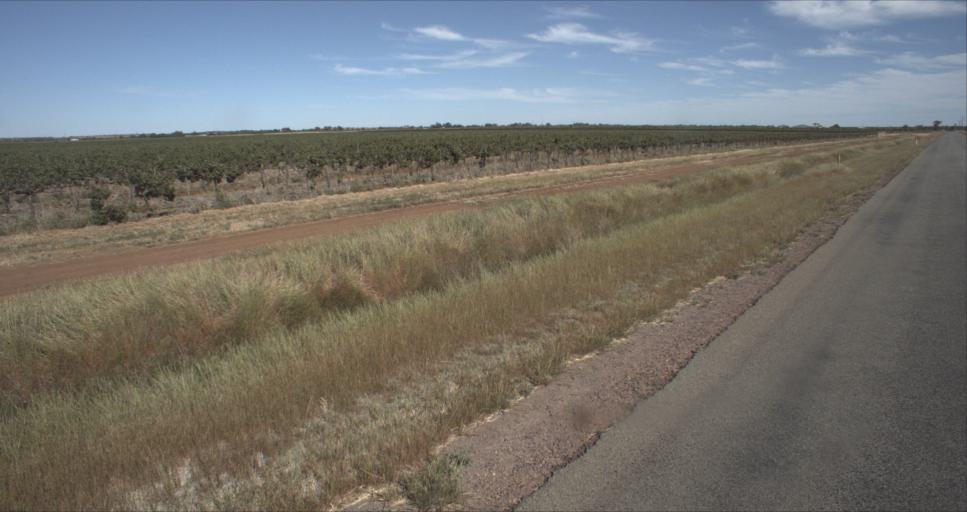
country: AU
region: New South Wales
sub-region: Leeton
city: Leeton
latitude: -34.5793
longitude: 146.3801
